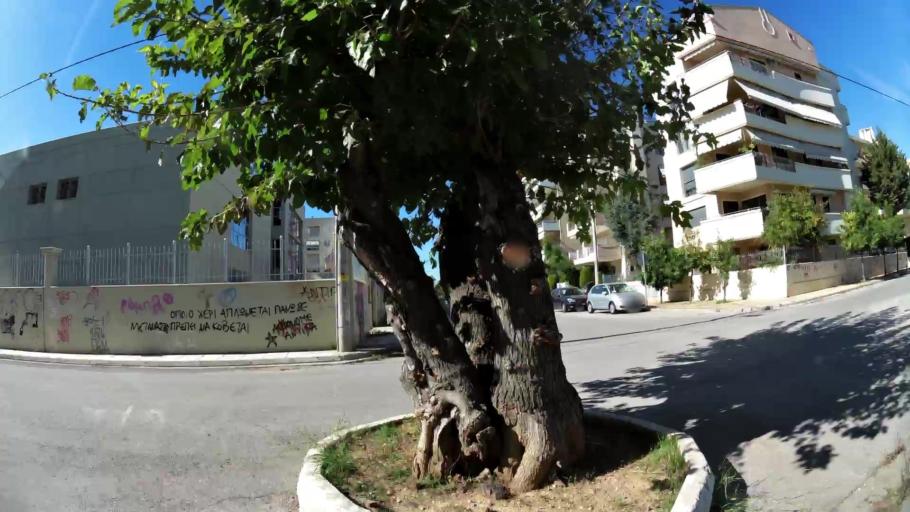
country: GR
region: Attica
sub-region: Nomarchia Athinas
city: Khalandrion
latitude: 38.0230
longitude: 23.8167
